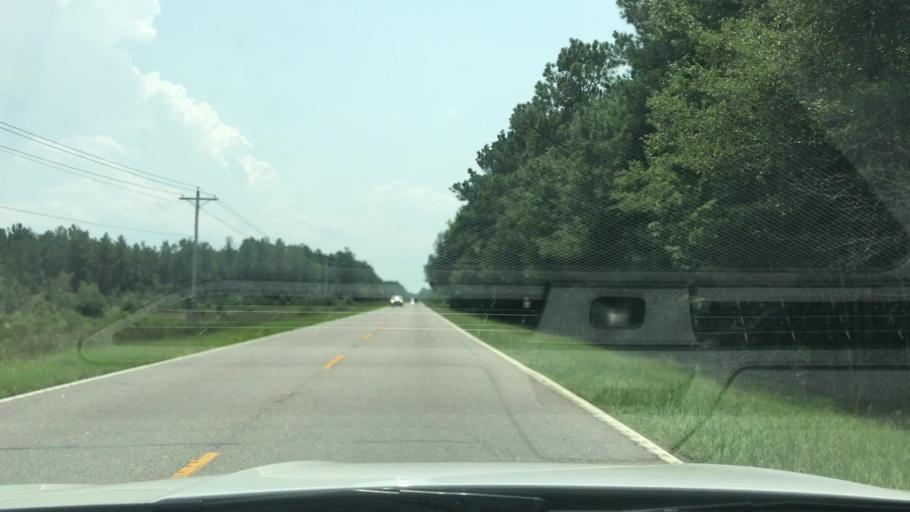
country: US
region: South Carolina
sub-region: Georgetown County
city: Georgetown
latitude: 33.5216
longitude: -79.2454
